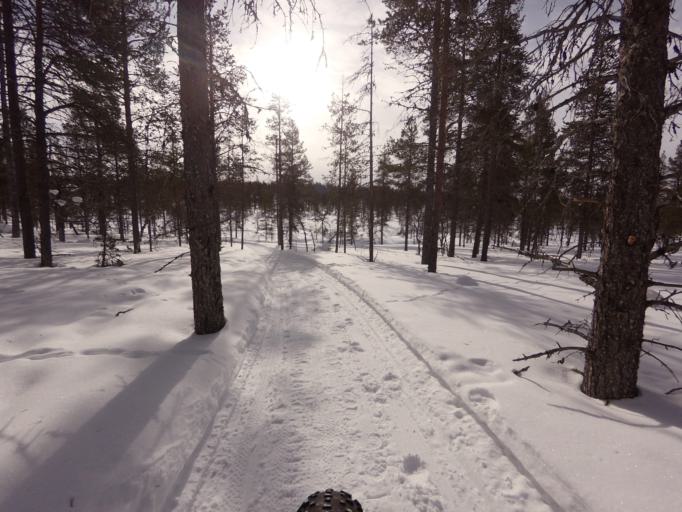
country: FI
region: Lapland
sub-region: Pohjois-Lappi
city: Ivalo
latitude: 68.3442
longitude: 27.4340
